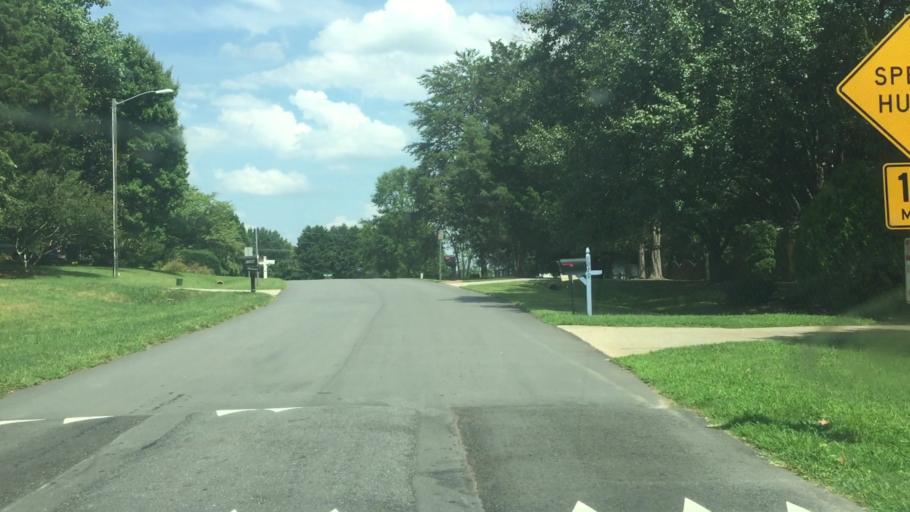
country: US
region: North Carolina
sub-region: Iredell County
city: Mooresville
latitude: 35.5514
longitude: -80.7920
